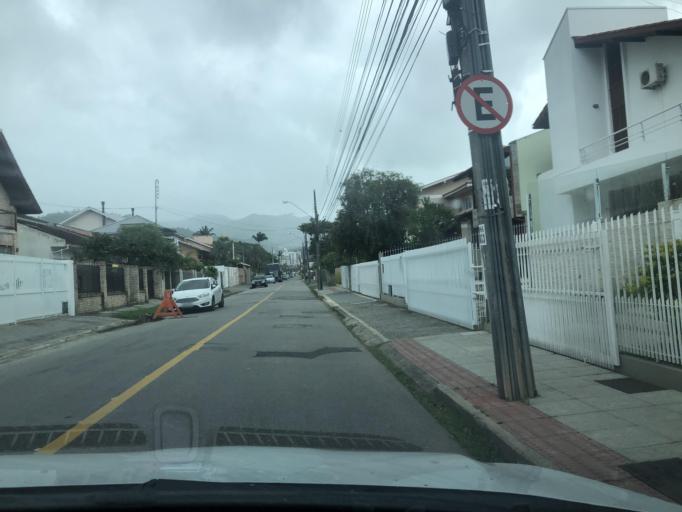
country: BR
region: Santa Catarina
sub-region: Florianopolis
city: Santa Monica
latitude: -27.5933
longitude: -48.5120
